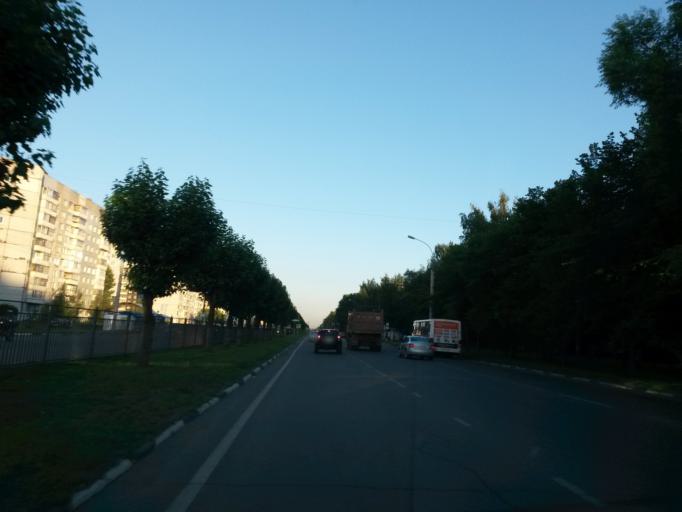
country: RU
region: Jaroslavl
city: Yaroslavl
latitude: 57.6933
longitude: 39.7717
